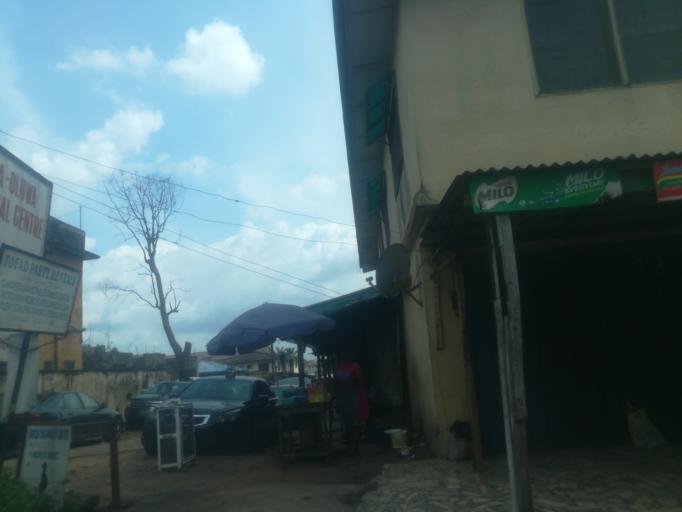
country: NG
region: Oyo
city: Ibadan
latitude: 7.3633
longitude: 3.8746
